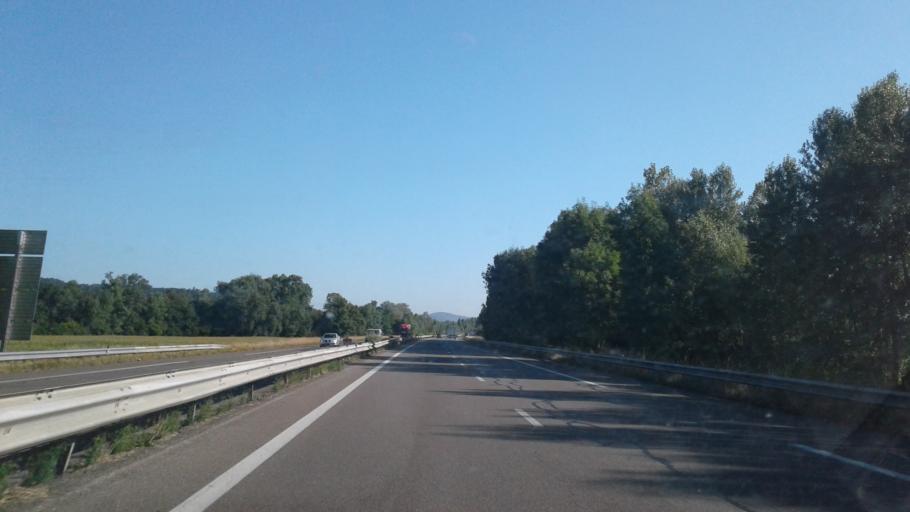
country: FR
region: Rhone-Alpes
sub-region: Departement de l'Ain
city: Priay
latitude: 46.0219
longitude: 5.3140
